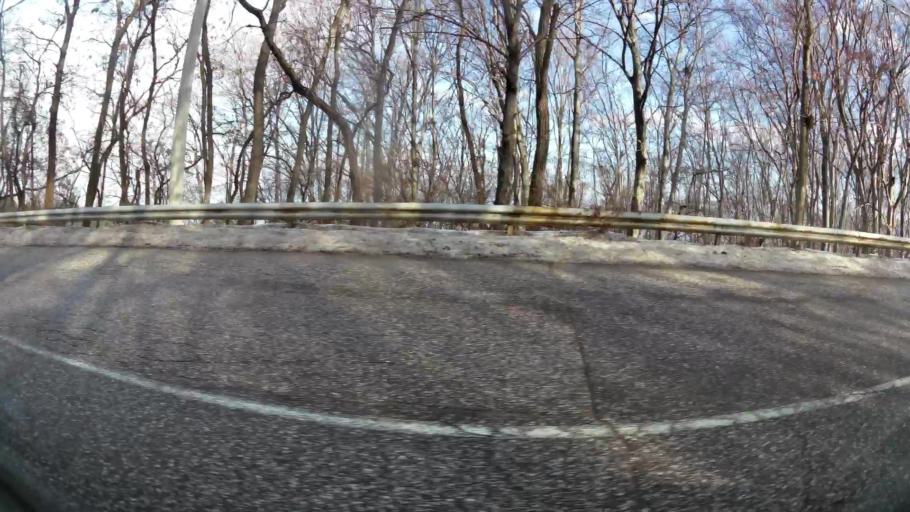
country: BG
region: Sofia-Capital
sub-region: Stolichna Obshtina
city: Sofia
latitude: 42.6465
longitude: 23.2497
